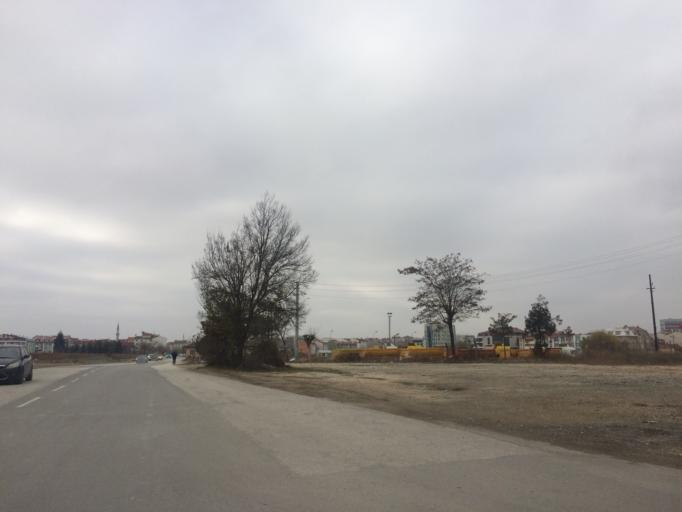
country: TR
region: Eskisehir
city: Eskisehir
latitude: 39.7801
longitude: 30.4952
